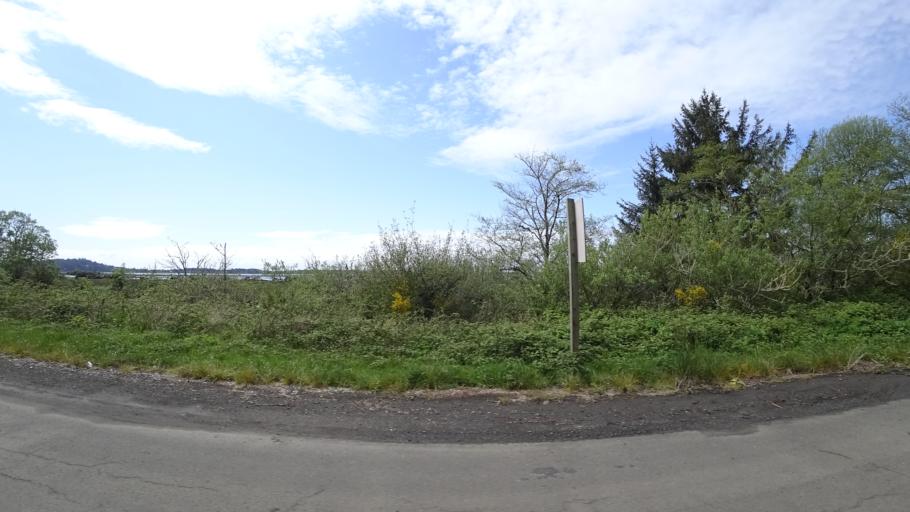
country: US
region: Oregon
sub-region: Lincoln County
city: Lincoln City
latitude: 44.9051
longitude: -124.0067
